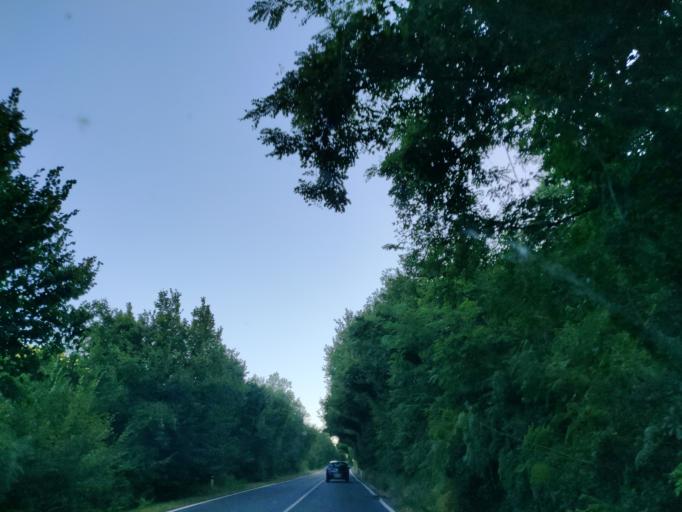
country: IT
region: Latium
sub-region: Provincia di Viterbo
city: Gradoli
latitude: 42.6552
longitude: 11.8467
